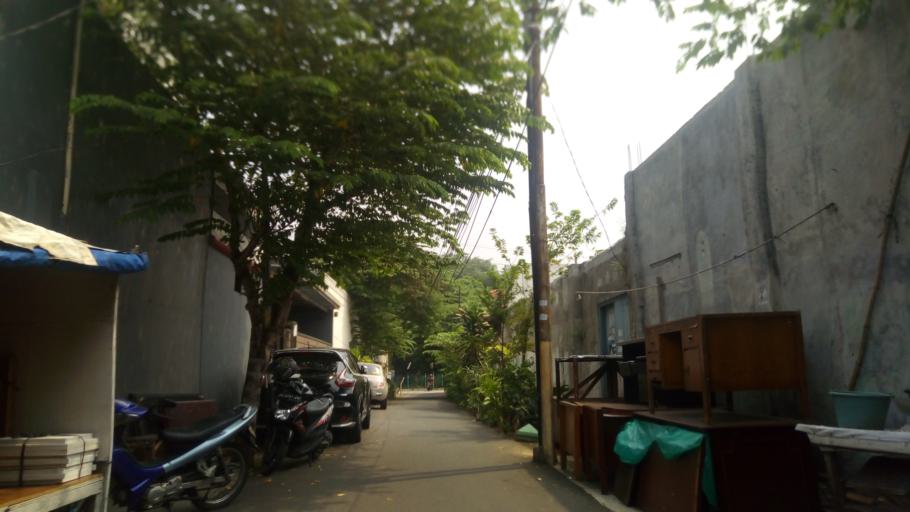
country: ID
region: Jakarta Raya
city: Jakarta
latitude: -6.1889
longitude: 106.8348
